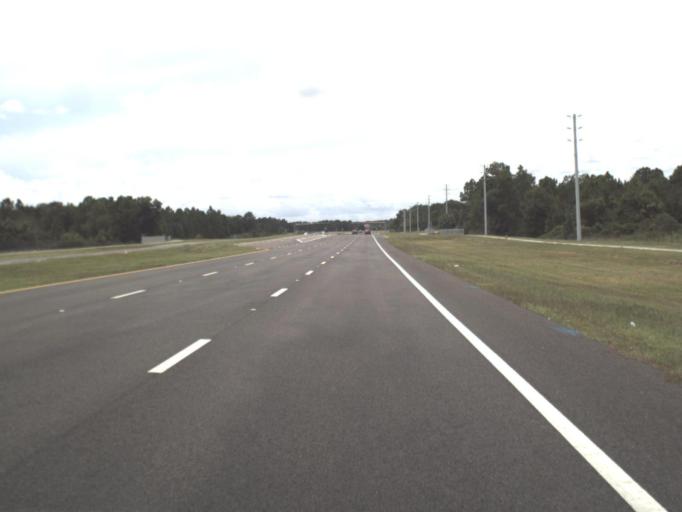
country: US
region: Florida
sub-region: Hillsborough County
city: Pebble Creek
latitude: 28.1916
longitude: -82.3390
